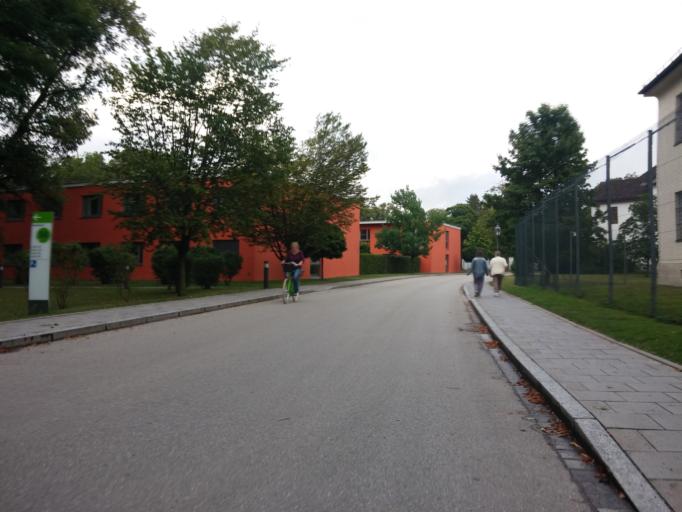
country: DE
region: Bavaria
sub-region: Upper Bavaria
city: Haar
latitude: 48.1190
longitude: 11.7483
